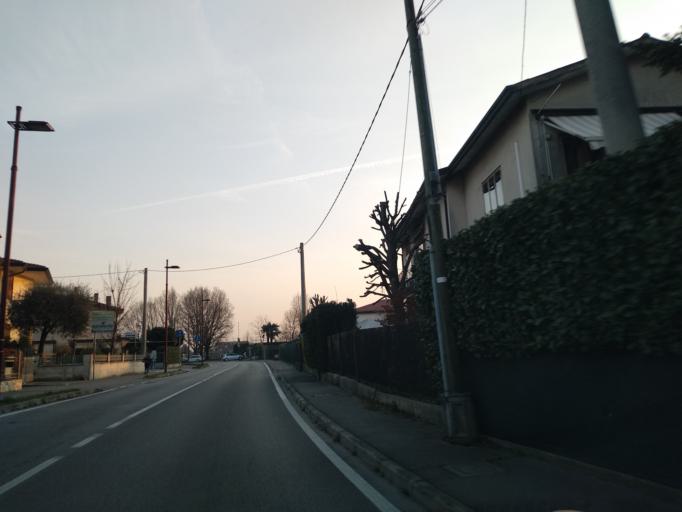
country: IT
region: Veneto
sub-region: Provincia di Padova
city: Sarmeola
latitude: 45.4307
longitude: 11.8088
